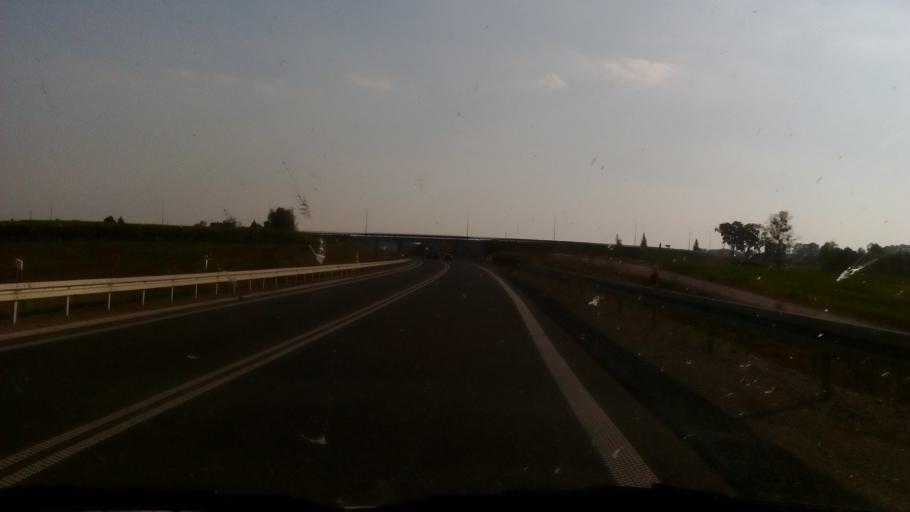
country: PL
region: Podlasie
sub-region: Powiat grajewski
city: Rajgrod
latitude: 53.7764
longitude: 22.8361
